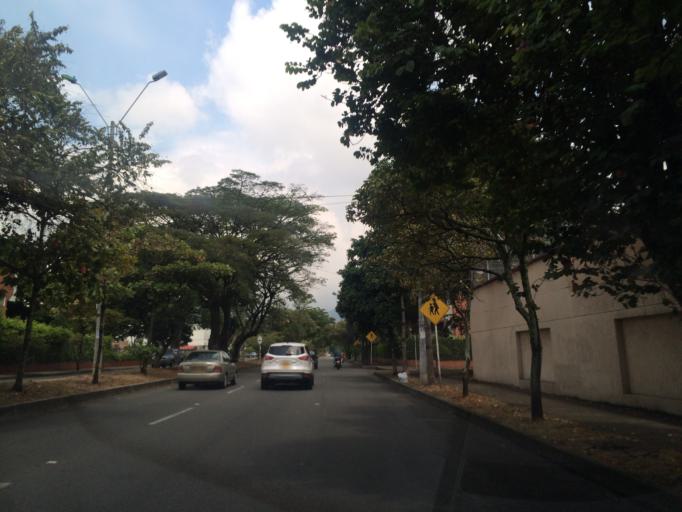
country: CO
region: Valle del Cauca
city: Cali
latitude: 3.3932
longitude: -76.5333
